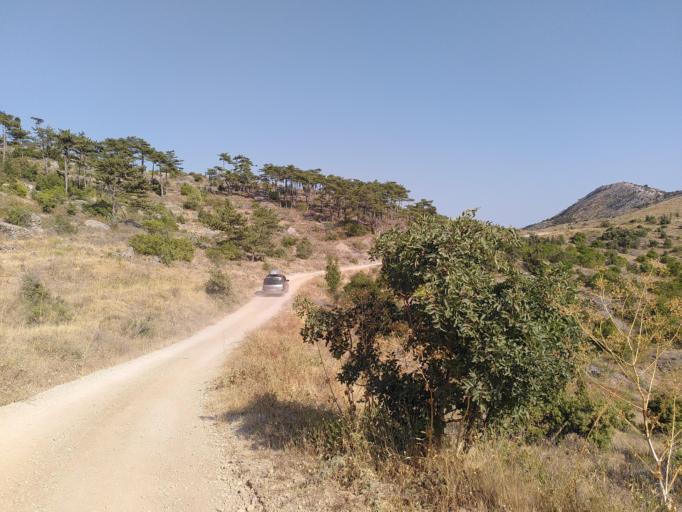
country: HR
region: Splitsko-Dalmatinska
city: Stari Grad
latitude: 43.1533
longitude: 16.5866
